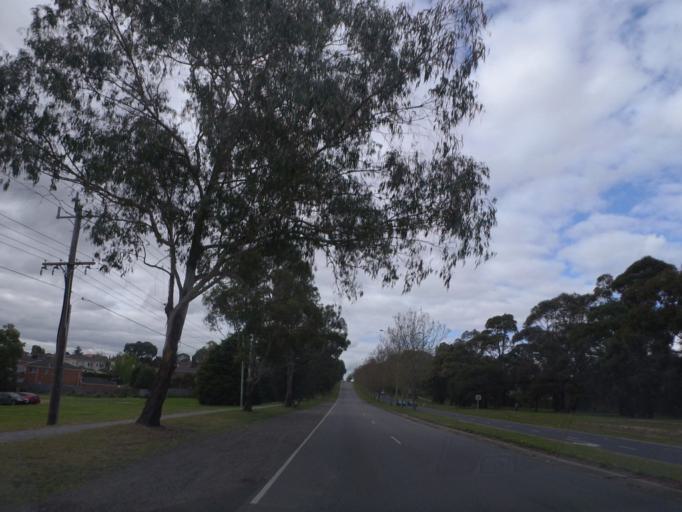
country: AU
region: Victoria
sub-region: Knox
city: Wantirna
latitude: -37.8547
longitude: 145.2181
